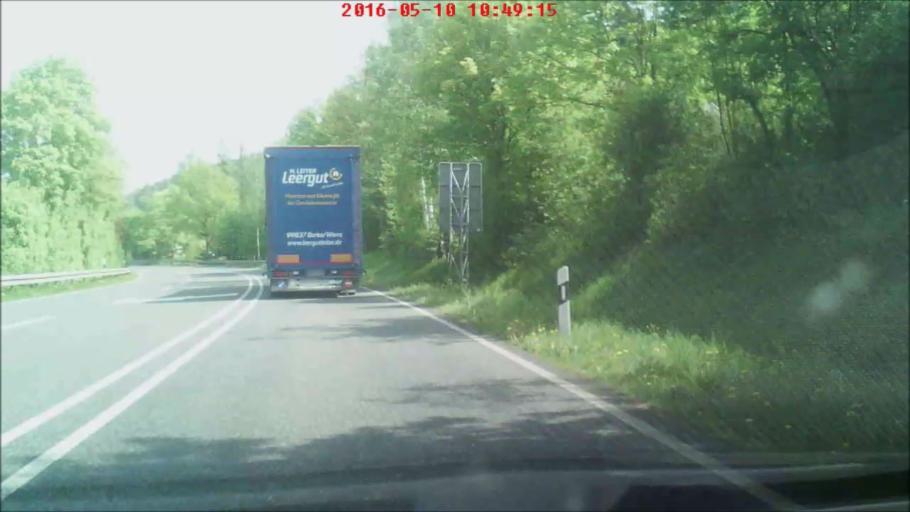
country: DE
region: Hesse
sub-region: Regierungsbezirk Kassel
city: Burghaun
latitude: 50.7664
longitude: 9.6950
